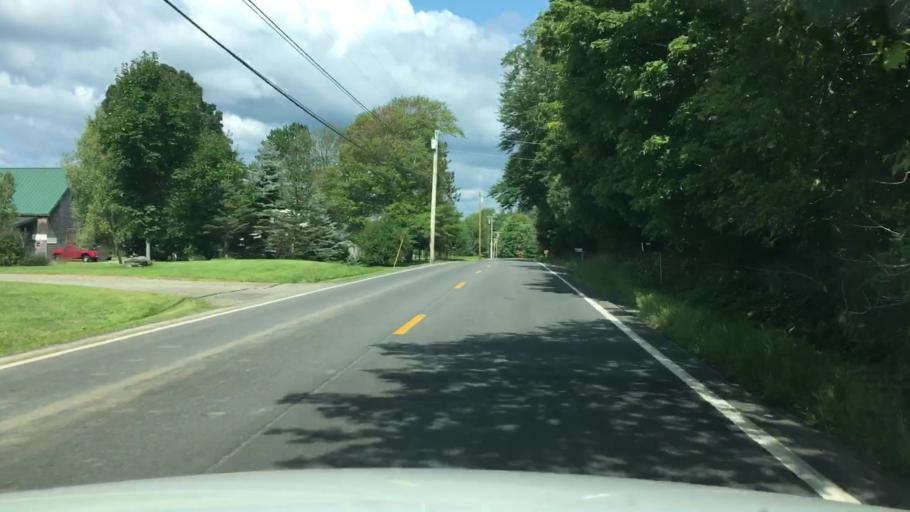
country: US
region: Maine
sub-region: Somerset County
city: Skowhegan
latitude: 44.7428
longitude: -69.6905
